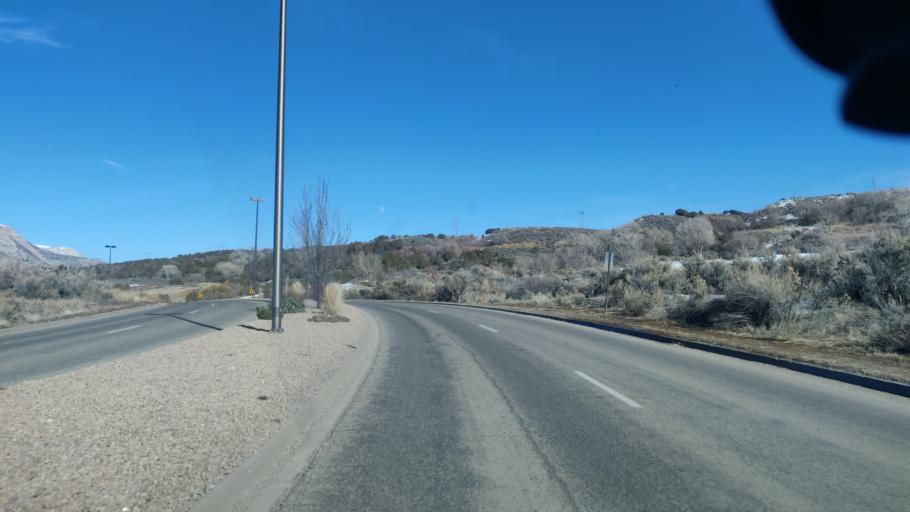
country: US
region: Colorado
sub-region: Garfield County
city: Battlement Mesa
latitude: 39.4482
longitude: -108.0338
